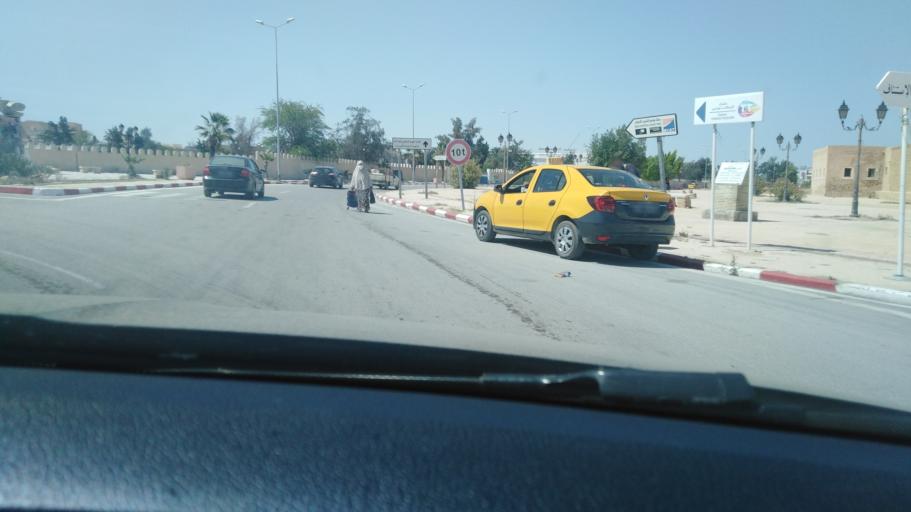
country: TN
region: Al Qayrawan
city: Kairouan
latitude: 35.6877
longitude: 10.1003
